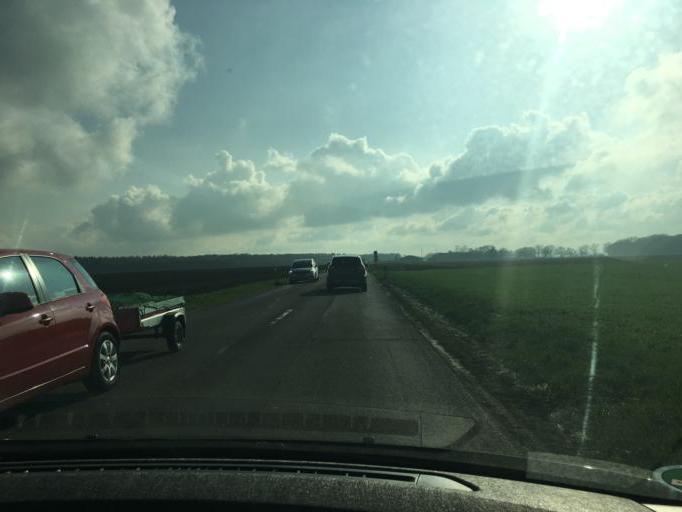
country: DE
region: North Rhine-Westphalia
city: Bornheim
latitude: 50.7343
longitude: 6.9463
